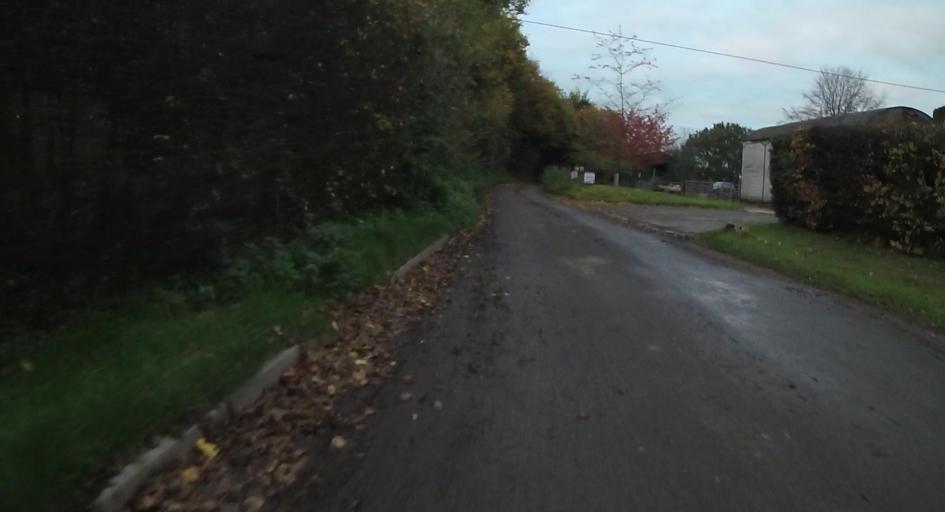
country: GB
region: England
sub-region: Hampshire
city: Kingsley
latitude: 51.1549
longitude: -0.8787
